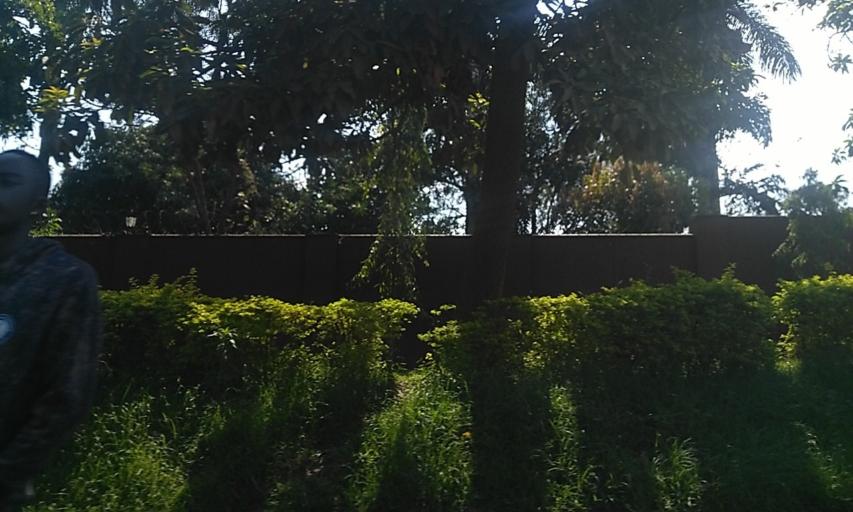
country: UG
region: Central Region
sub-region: Wakiso District
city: Kireka
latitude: 0.3617
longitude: 32.6076
